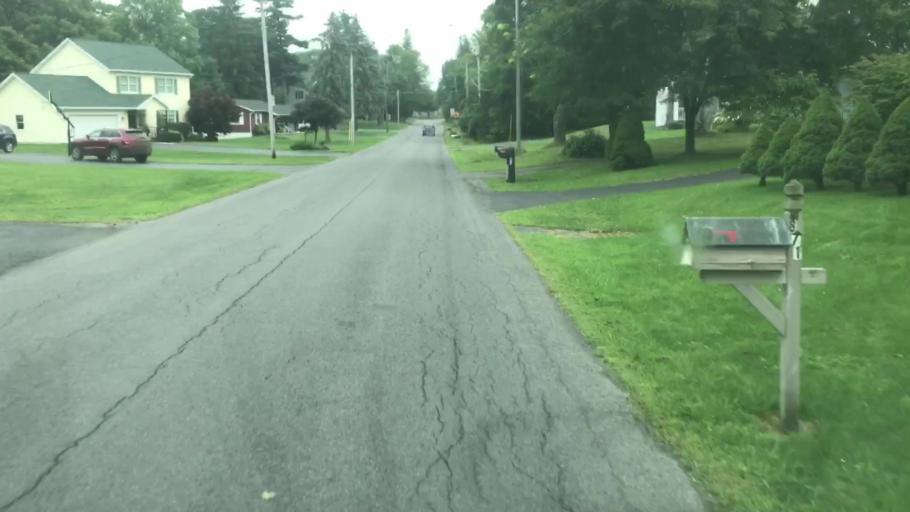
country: US
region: New York
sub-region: Onondaga County
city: Skaneateles
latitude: 42.9462
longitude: -76.4423
